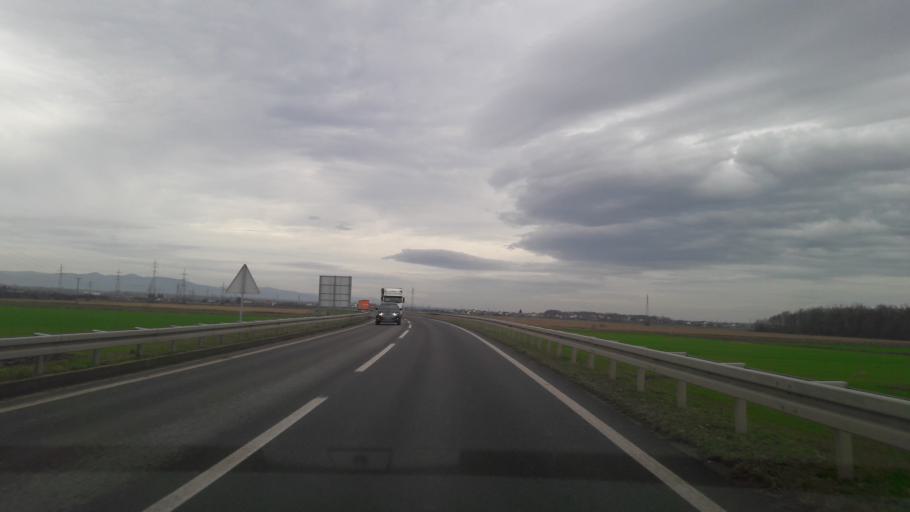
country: HR
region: Osjecko-Baranjska
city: Velimirovac
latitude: 45.5099
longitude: 18.1133
